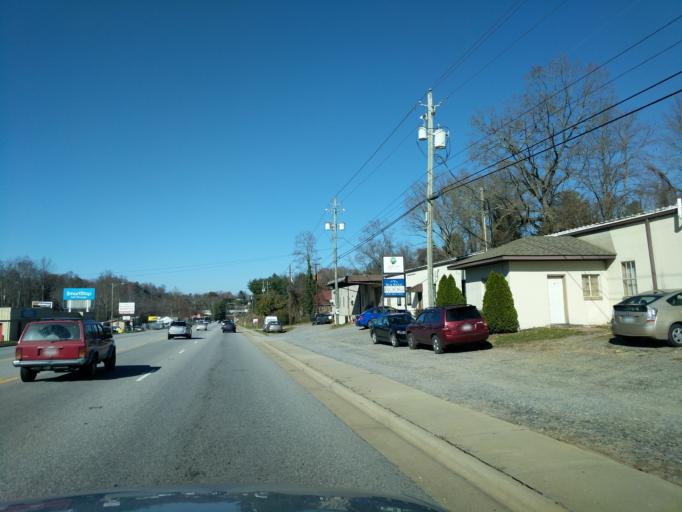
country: US
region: North Carolina
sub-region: Buncombe County
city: Biltmore Forest
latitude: 35.5405
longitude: -82.5206
